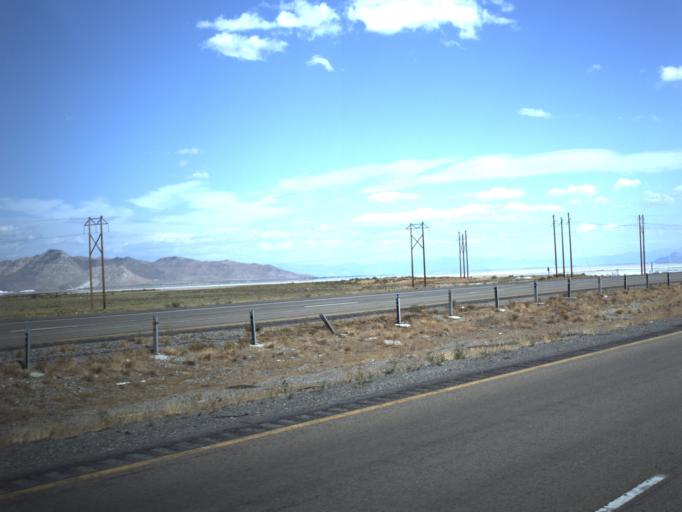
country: US
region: Utah
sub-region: Tooele County
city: Grantsville
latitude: 40.7439
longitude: -112.6351
